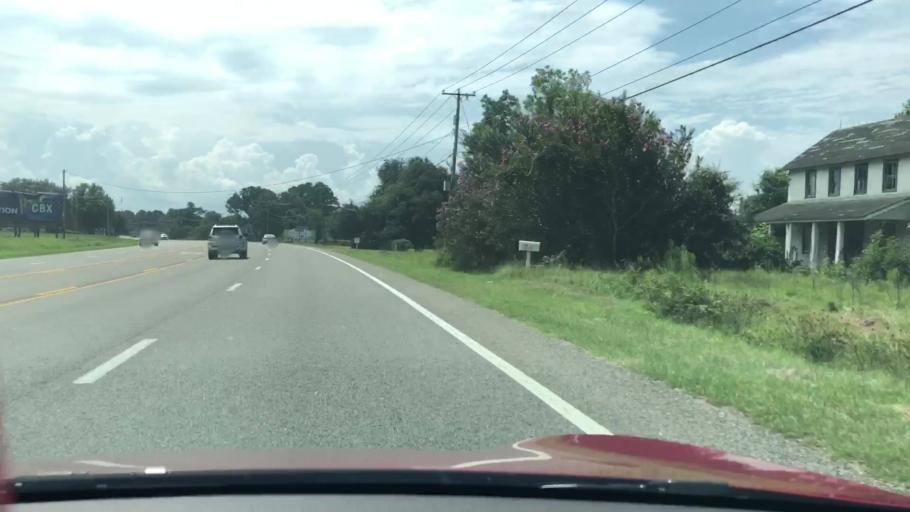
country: US
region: North Carolina
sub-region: Dare County
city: Southern Shores
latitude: 36.1305
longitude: -75.8379
